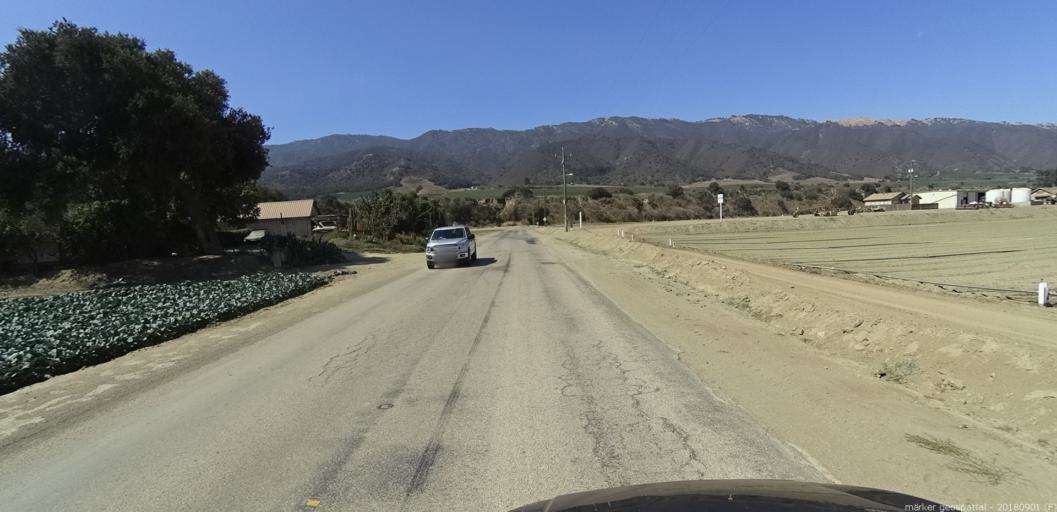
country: US
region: California
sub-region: Monterey County
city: Gonzales
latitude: 36.4797
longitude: -121.4767
